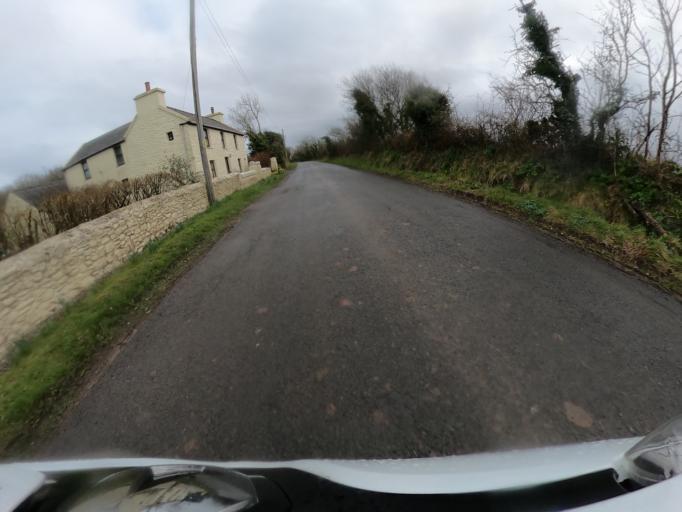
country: IM
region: Ramsey
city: Ramsey
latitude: 54.3758
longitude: -4.4457
